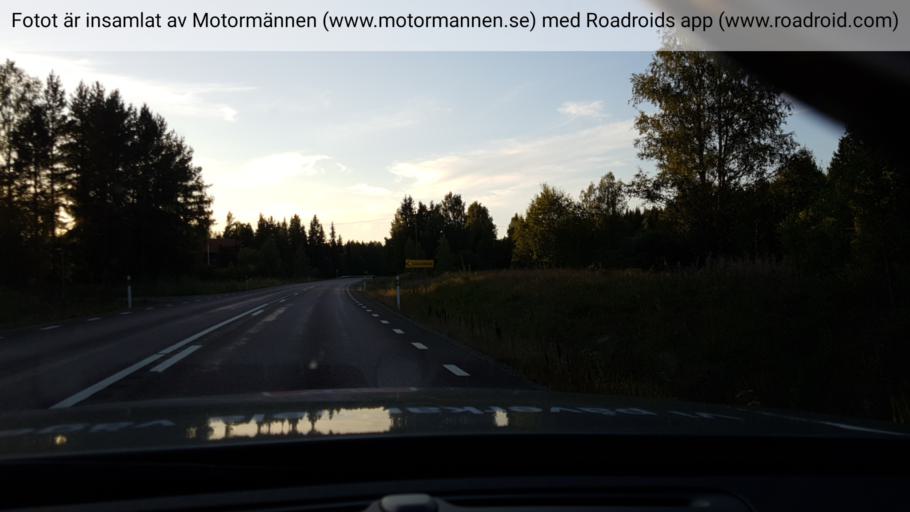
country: SE
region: Vaermland
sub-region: Storfors Kommun
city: Storfors
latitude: 59.4699
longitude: 14.3326
